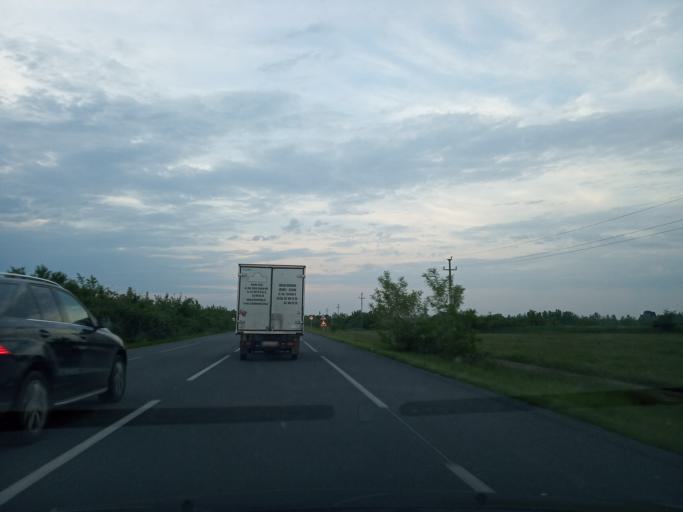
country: RO
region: Timis
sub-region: Oras Deta
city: Deta
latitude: 45.3879
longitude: 21.2319
